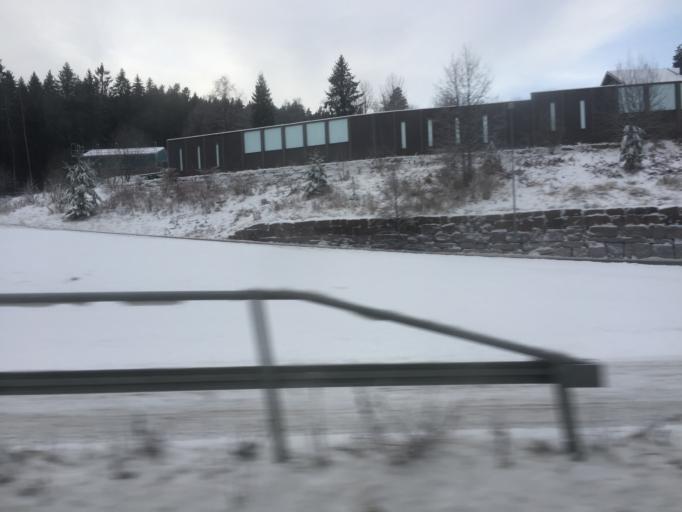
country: NO
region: Akershus
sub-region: Oppegard
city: Kolbotn
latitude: 59.7526
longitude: 10.7819
